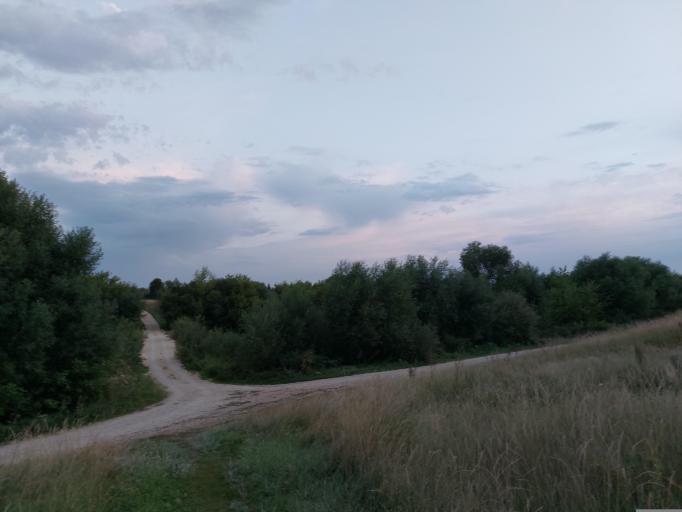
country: RU
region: Lipetsk
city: Dolgorukovo
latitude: 52.3749
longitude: 38.0581
